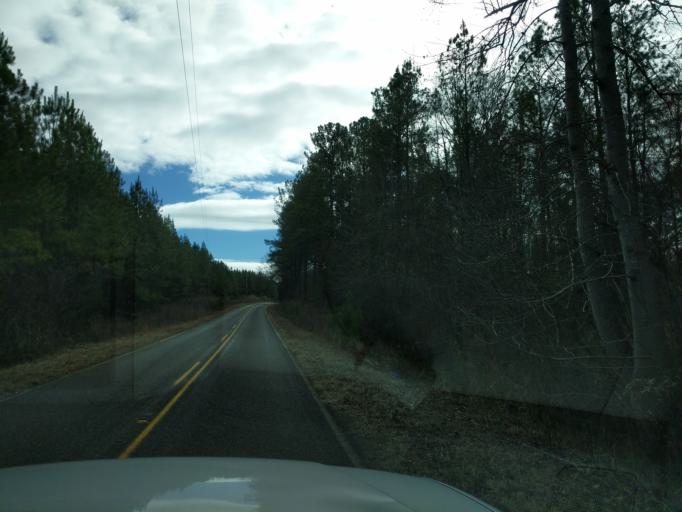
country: US
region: South Carolina
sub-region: Edgefield County
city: Edgefield
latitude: 33.9116
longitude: -82.0040
